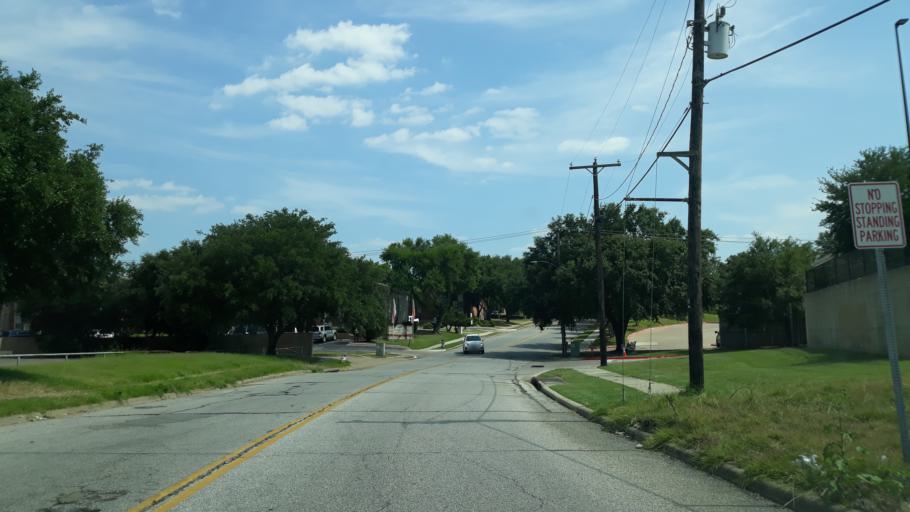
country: US
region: Texas
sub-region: Dallas County
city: Irving
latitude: 32.8348
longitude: -97.0038
